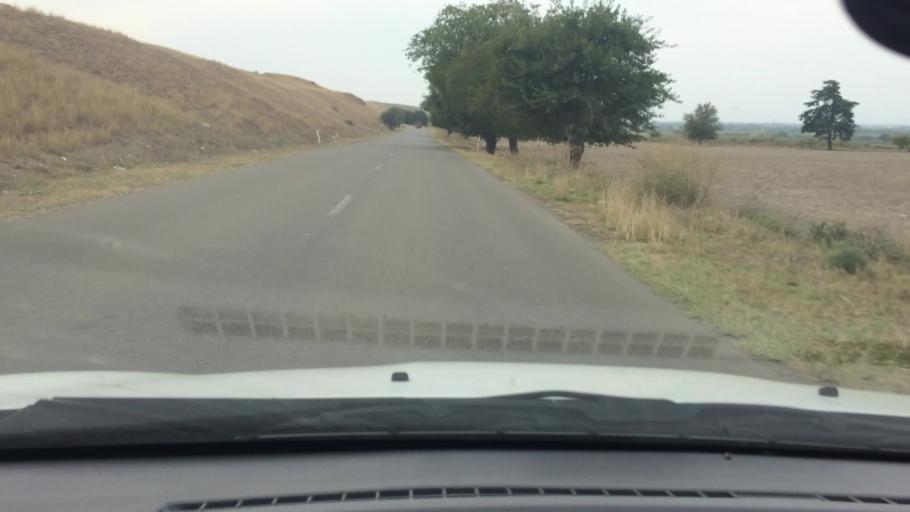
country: AM
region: Tavush
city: Berdavan
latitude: 41.3381
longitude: 45.0062
